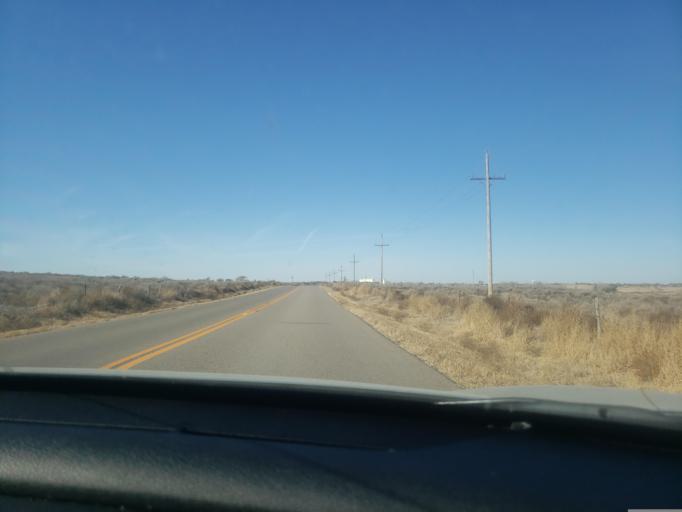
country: US
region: Kansas
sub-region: Finney County
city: Garden City
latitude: 37.9486
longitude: -100.8502
